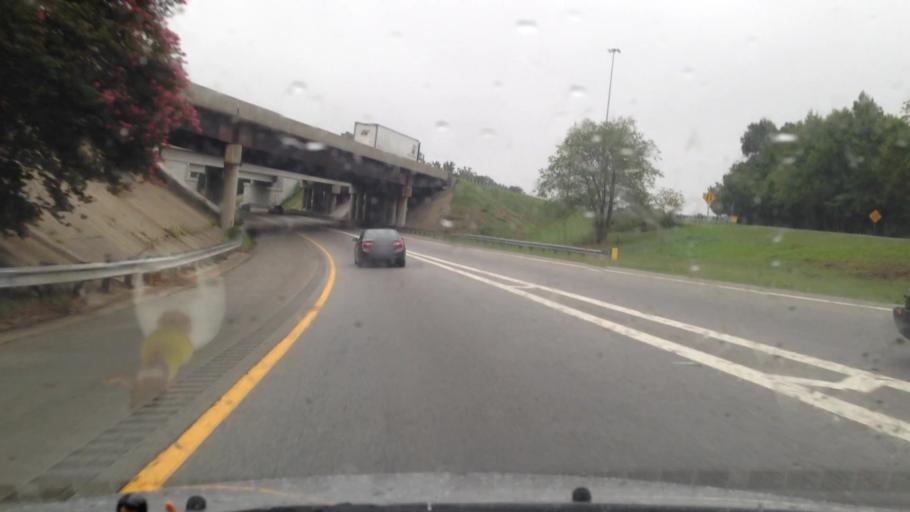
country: US
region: North Carolina
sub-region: Guilford County
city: Greensboro
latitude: 36.0455
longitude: -79.7706
